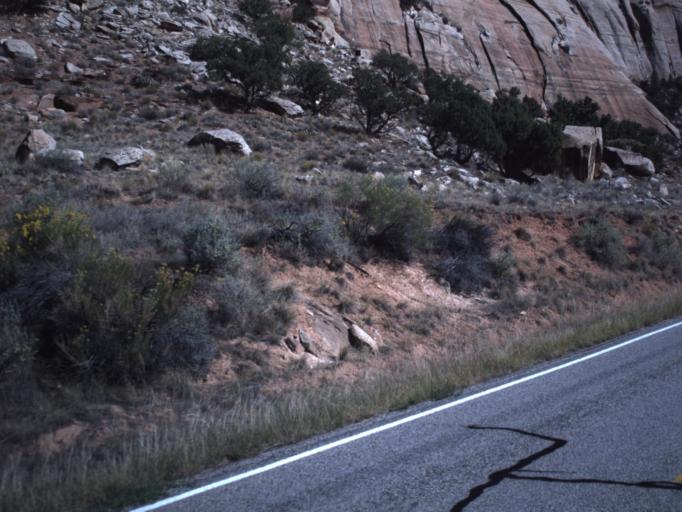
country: US
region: Utah
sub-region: San Juan County
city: Monticello
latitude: 38.0322
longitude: -109.5419
